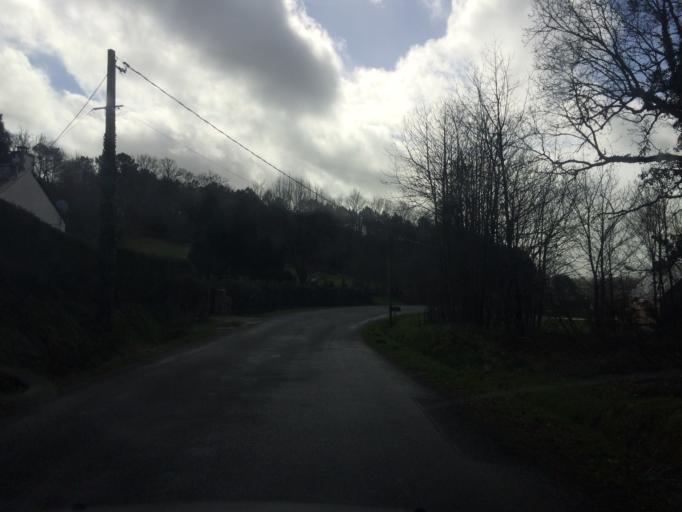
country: FR
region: Brittany
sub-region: Departement du Morbihan
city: Saint-Jean-la-Poterie
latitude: 47.6281
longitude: -2.1156
